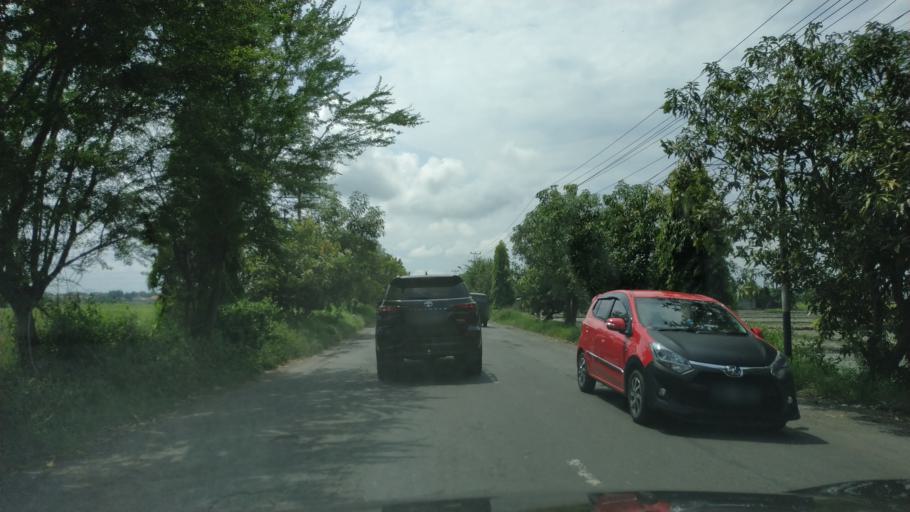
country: ID
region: Central Java
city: Adiwerna
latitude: -6.9182
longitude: 109.1264
